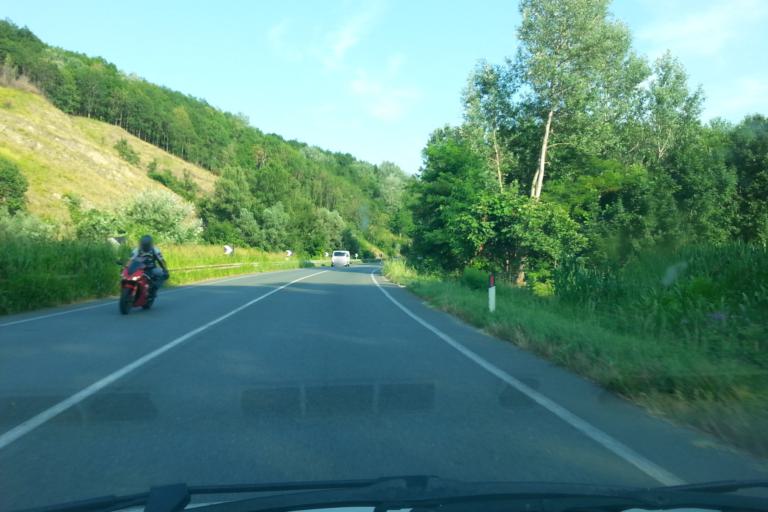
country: IT
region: Piedmont
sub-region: Provincia di Torino
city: Sant'Ambrogio di Torino
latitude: 45.1105
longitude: 7.3680
